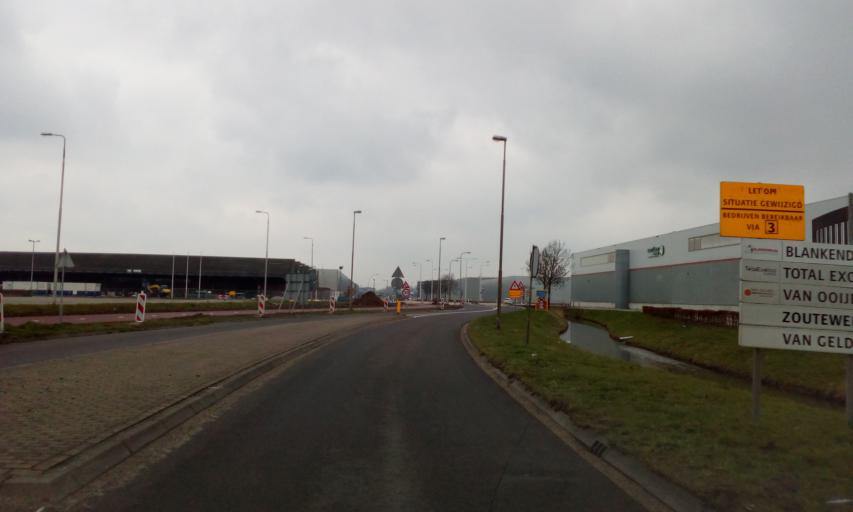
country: NL
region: South Holland
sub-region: Gemeente Zwijndrecht
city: Heerjansdam
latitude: 51.8579
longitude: 4.5612
